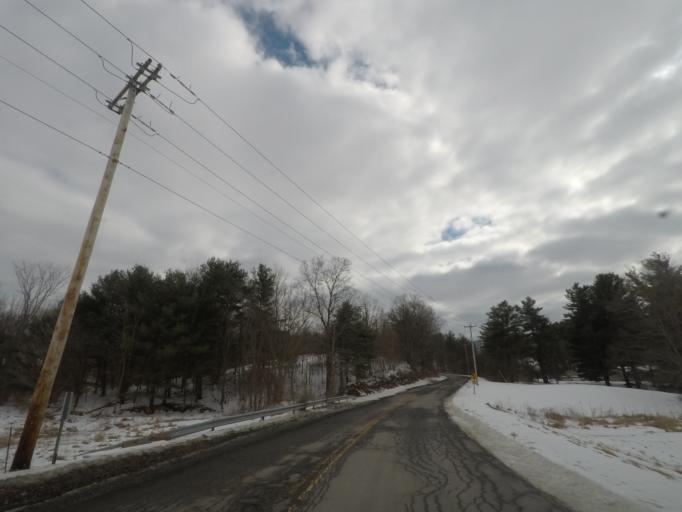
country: US
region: New York
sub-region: Rensselaer County
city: Hoosick Falls
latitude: 42.9193
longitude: -73.4306
